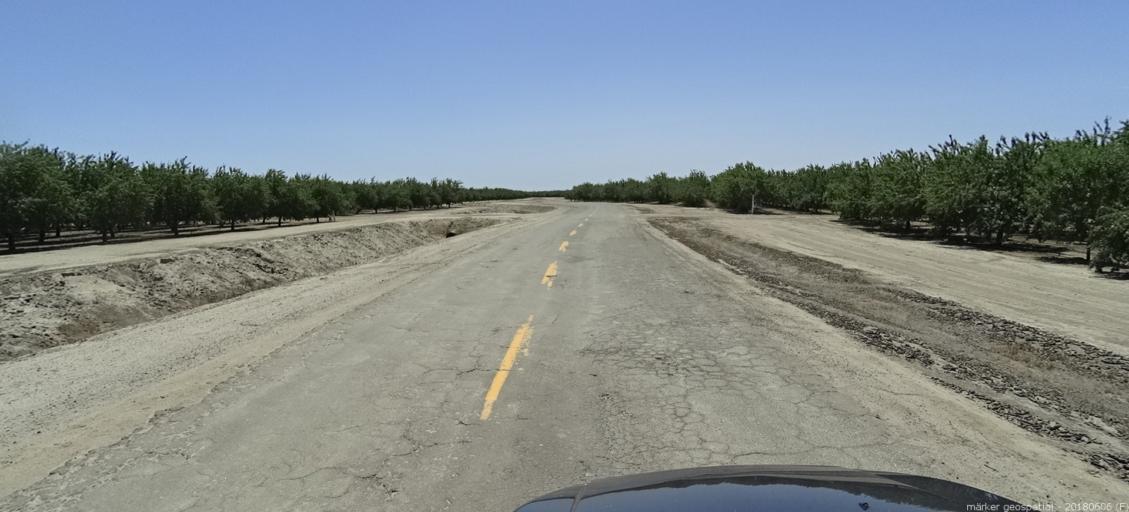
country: US
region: California
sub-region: Fresno County
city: Mendota
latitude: 36.8228
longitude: -120.3705
